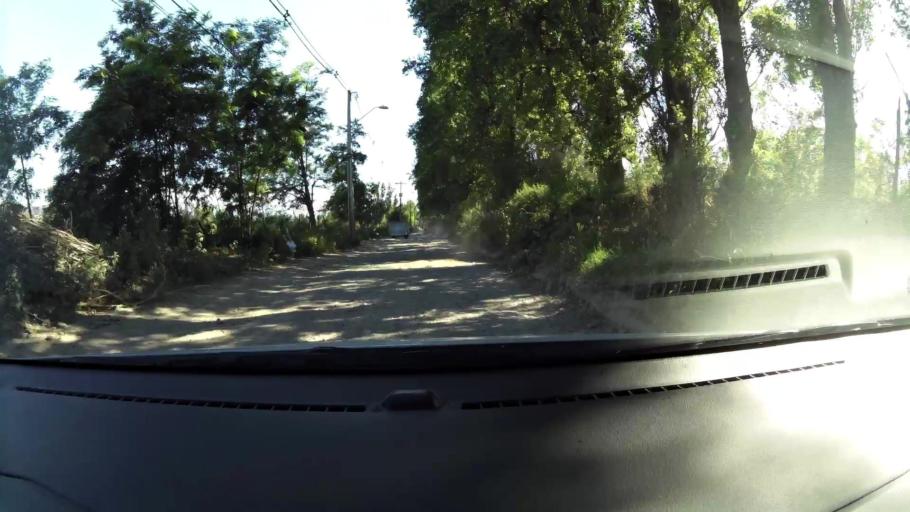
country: CL
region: Santiago Metropolitan
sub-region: Provincia de Maipo
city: San Bernardo
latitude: -33.5559
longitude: -70.7700
